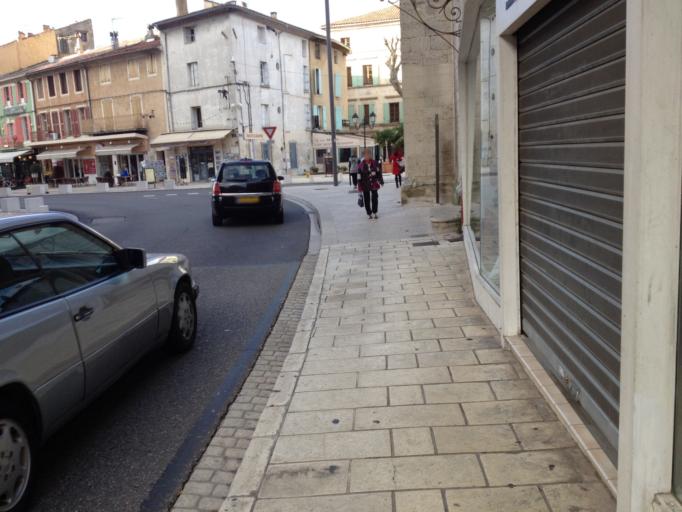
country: FR
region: Provence-Alpes-Cote d'Azur
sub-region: Departement du Vaucluse
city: Orange
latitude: 44.1360
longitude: 4.8095
